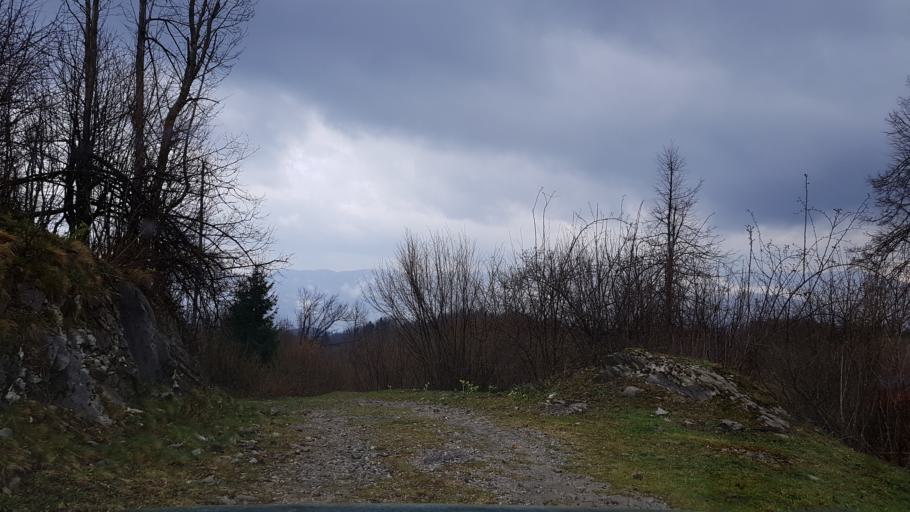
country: SI
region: Cerkno
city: Cerkno
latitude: 46.1431
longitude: 13.8671
